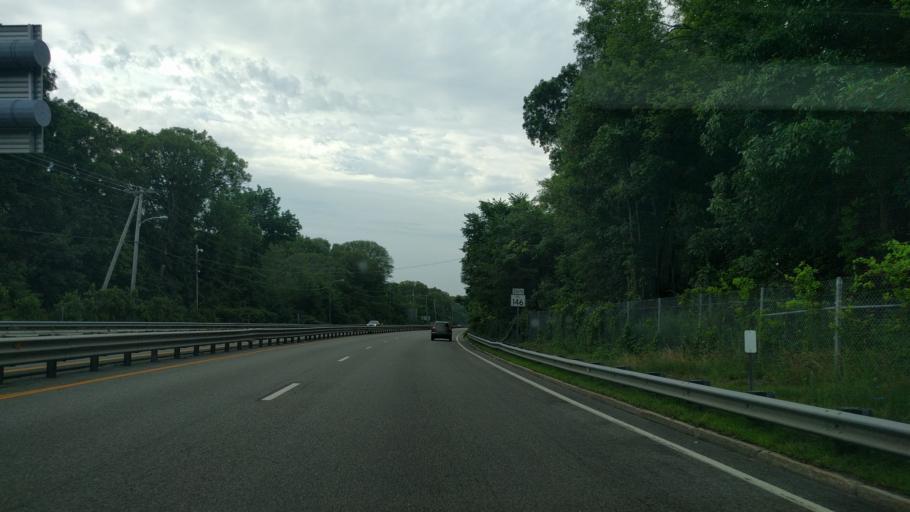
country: US
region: Rhode Island
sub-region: Providence County
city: Cumberland Hill
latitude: 41.9325
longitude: -71.4641
